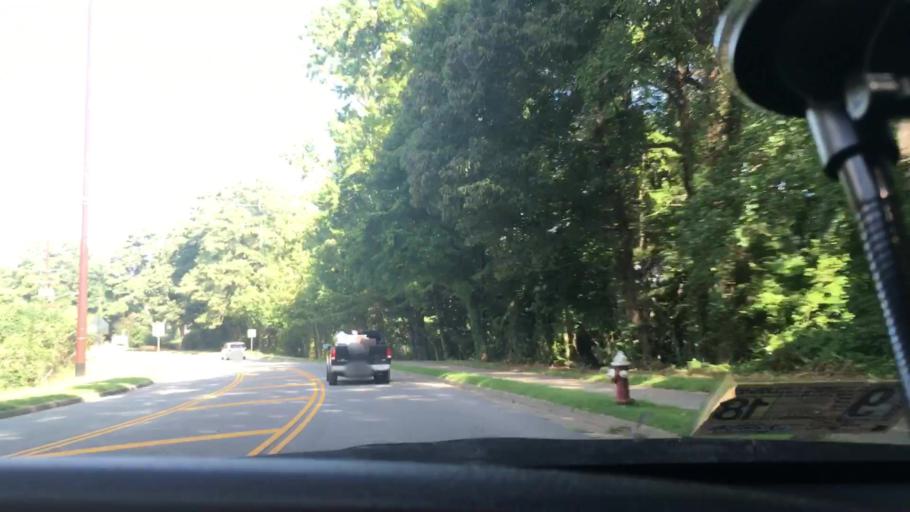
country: US
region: Virginia
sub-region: City of Virginia Beach
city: Virginia Beach
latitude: 36.8792
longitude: -76.0339
